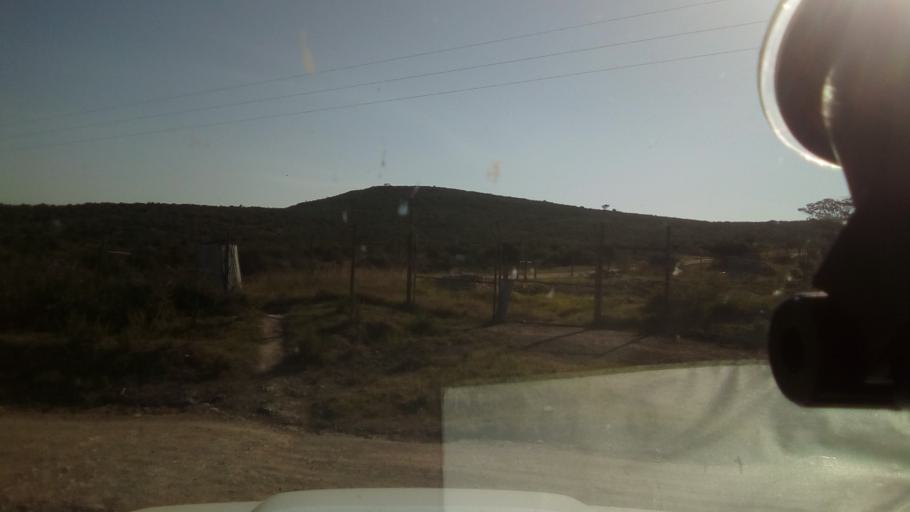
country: ZA
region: Eastern Cape
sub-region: Buffalo City Metropolitan Municipality
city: Bhisho
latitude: -32.8187
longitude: 27.3522
